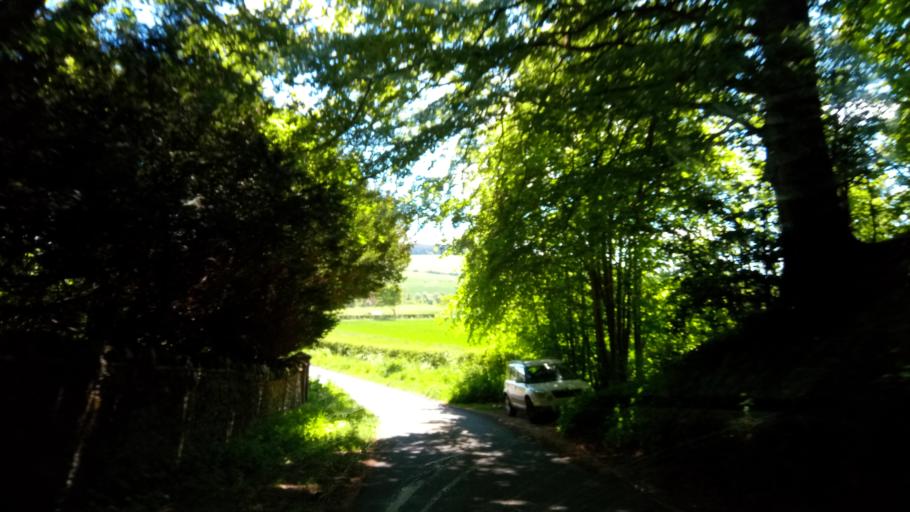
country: GB
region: Scotland
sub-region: The Scottish Borders
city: Saint Boswells
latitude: 55.4694
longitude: -2.6757
